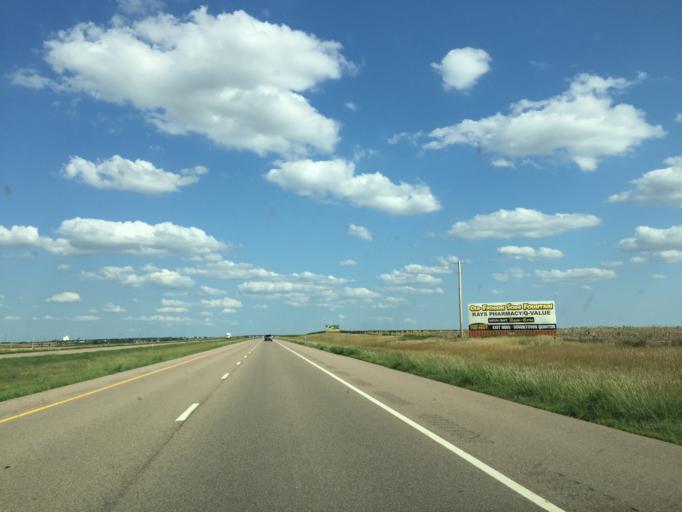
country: US
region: Kansas
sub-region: Gove County
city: Gove
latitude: 39.0825
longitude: -100.2943
